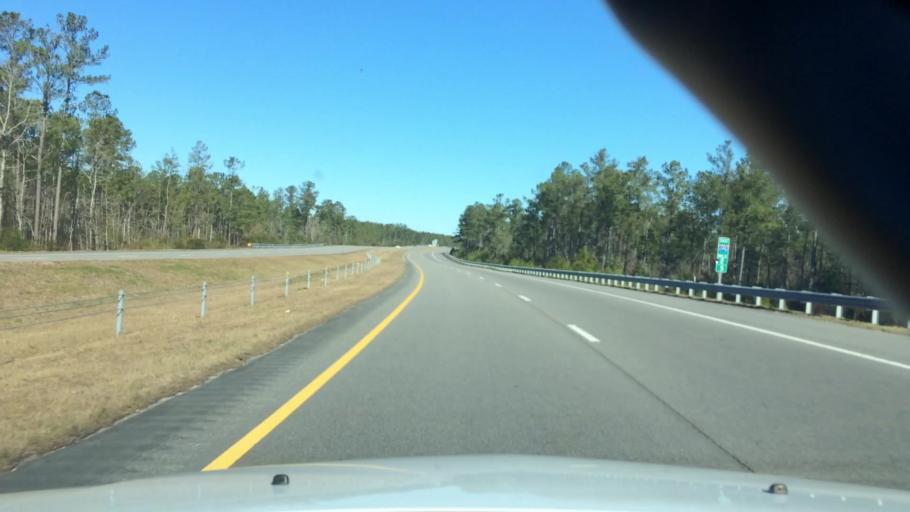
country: US
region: North Carolina
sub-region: Brunswick County
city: Leland
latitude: 34.2117
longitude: -78.0763
